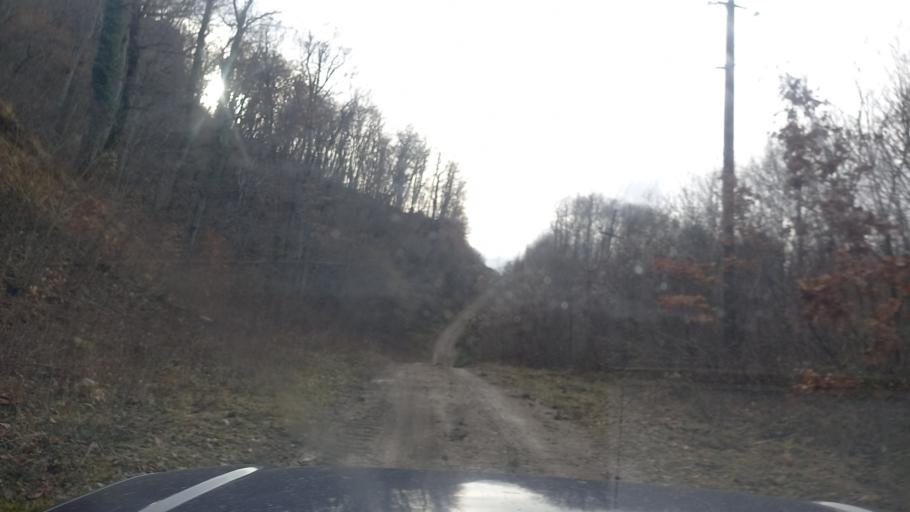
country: RU
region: Krasnodarskiy
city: Neftegorsk
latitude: 44.2065
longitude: 39.7083
